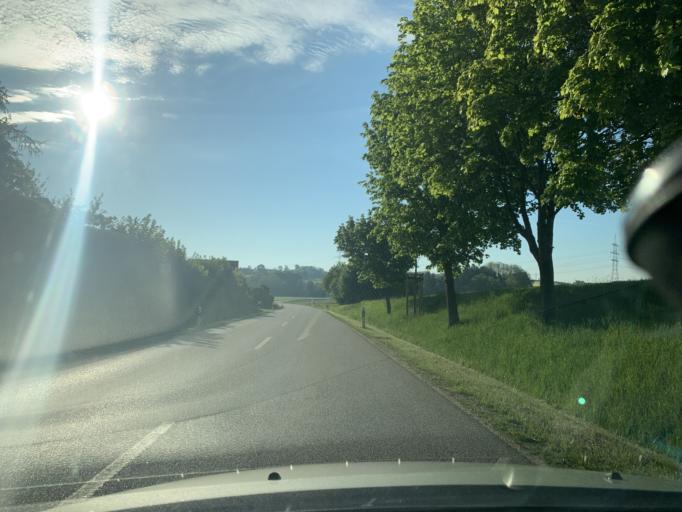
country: DE
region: Bavaria
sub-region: Lower Bavaria
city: Adlkofen
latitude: 48.5319
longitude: 12.2511
